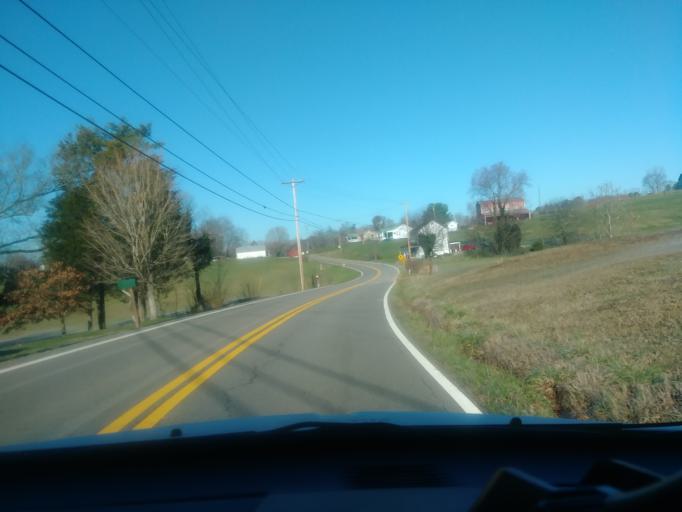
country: US
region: Tennessee
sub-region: Greene County
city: Mosheim
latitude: 36.1163
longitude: -82.9637
